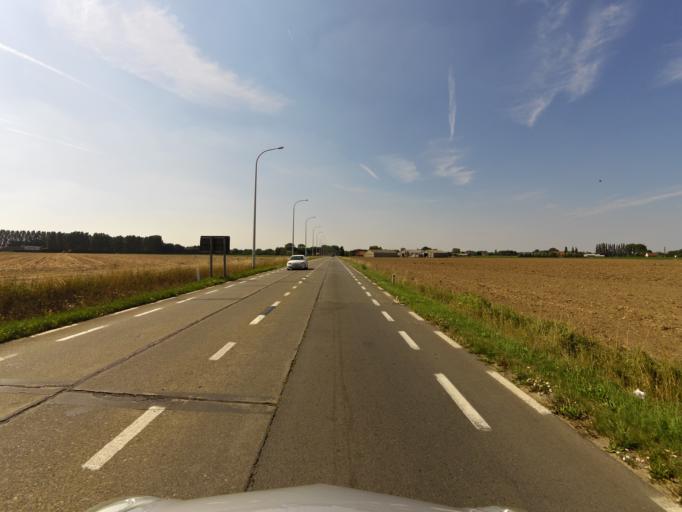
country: BE
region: Flanders
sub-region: Provincie West-Vlaanderen
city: Dentergem
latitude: 50.9890
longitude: 3.4573
